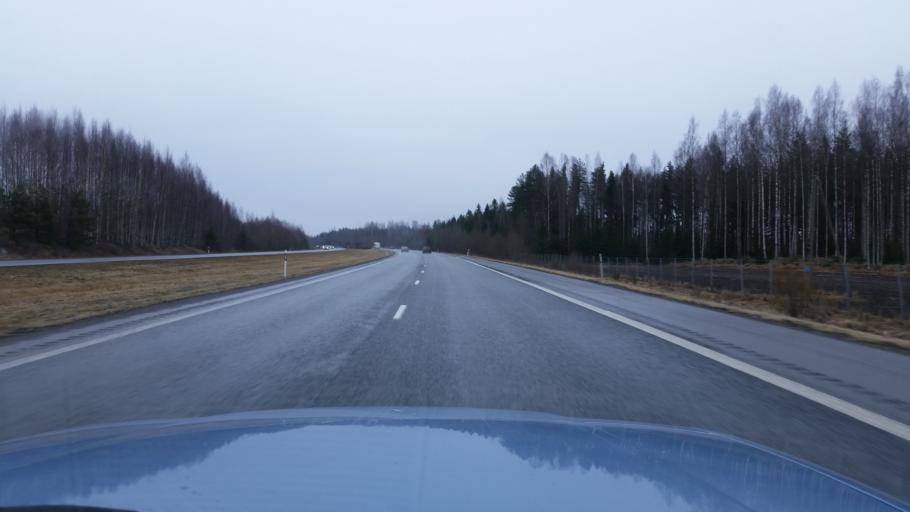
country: FI
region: Haeme
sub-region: Haemeenlinna
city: Kalvola
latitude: 61.0838
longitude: 24.2021
